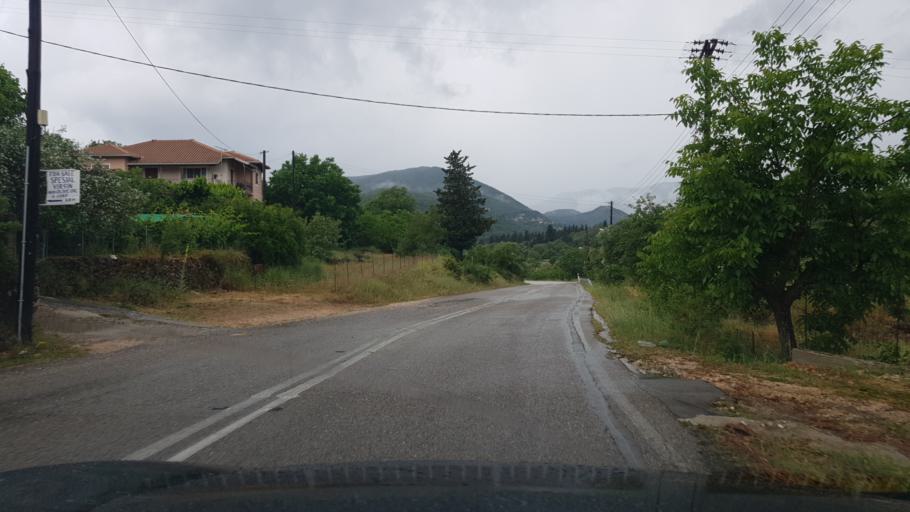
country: GR
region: Ionian Islands
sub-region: Lefkada
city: Nidri
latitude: 38.6327
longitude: 20.6537
